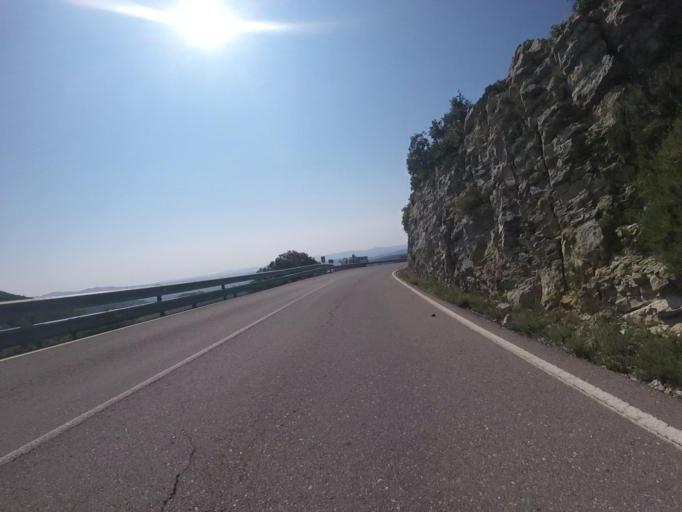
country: ES
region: Valencia
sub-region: Provincia de Castello
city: Benafigos
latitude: 40.2650
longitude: -0.2330
